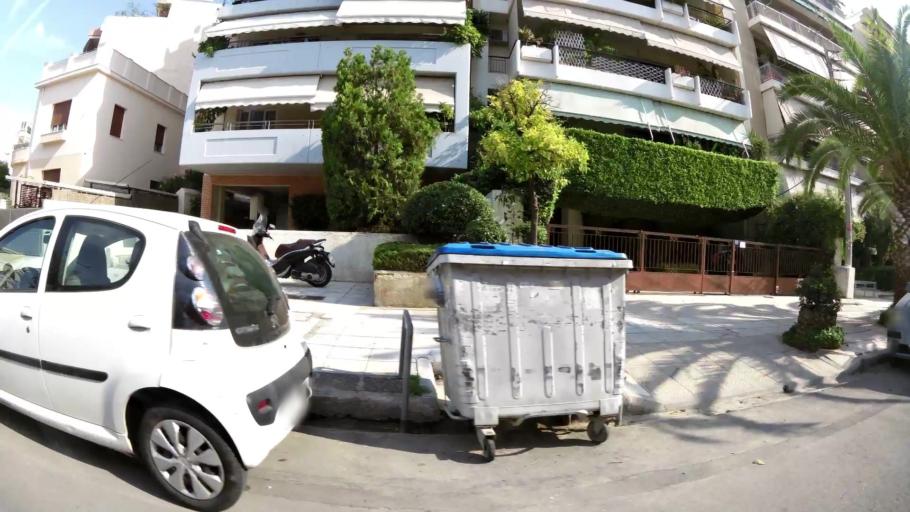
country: GR
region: Attica
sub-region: Nomarchia Athinas
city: Nea Smyrni
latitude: 37.9405
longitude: 23.7109
